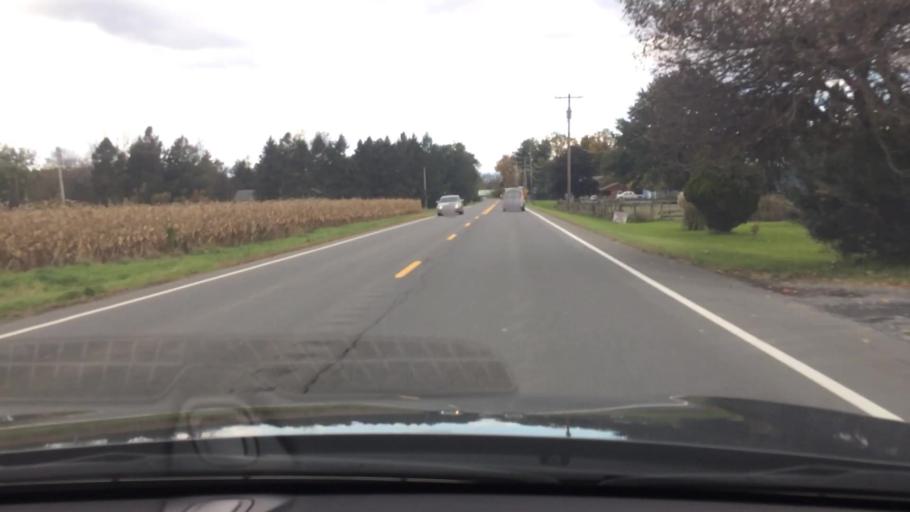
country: US
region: New York
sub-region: Columbia County
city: Oakdale
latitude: 42.1946
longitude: -73.7470
